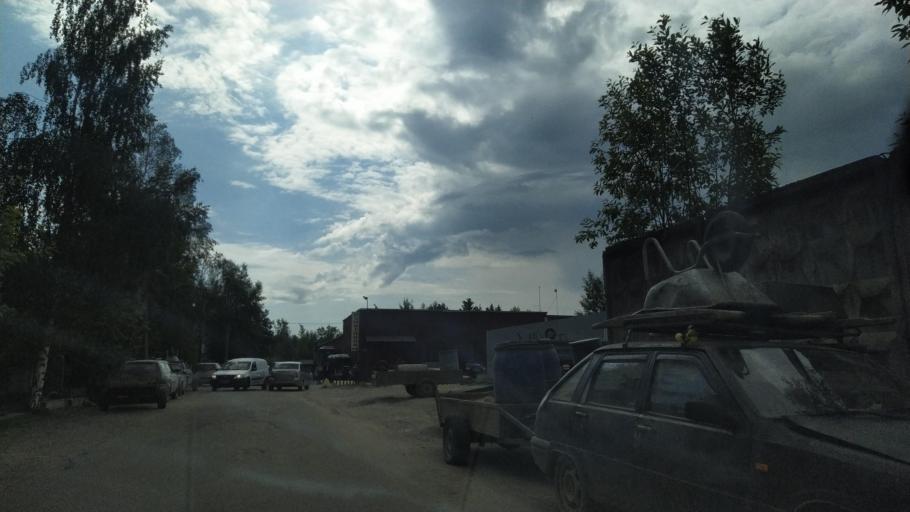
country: RU
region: St.-Petersburg
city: Aleksandrovskaya
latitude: 59.7635
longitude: 30.2650
